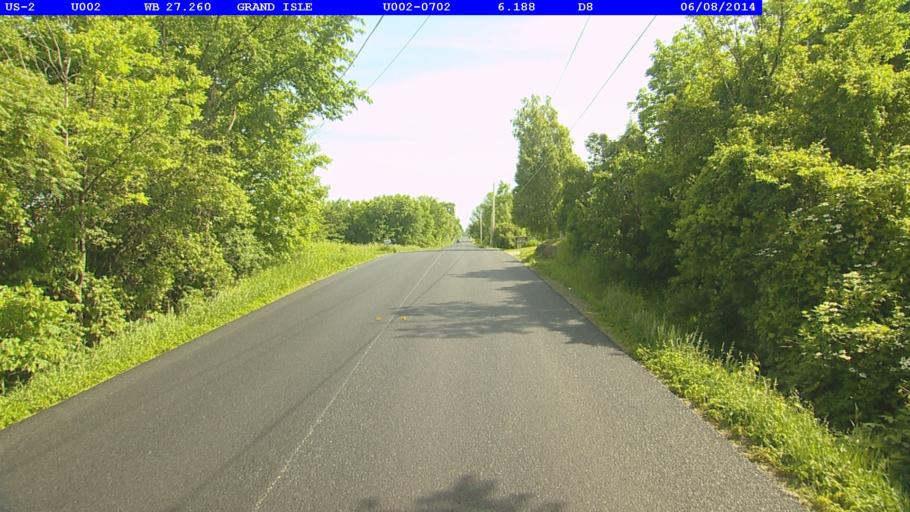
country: US
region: New York
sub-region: Clinton County
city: Cumberland Head
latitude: 44.6813
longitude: -73.3151
